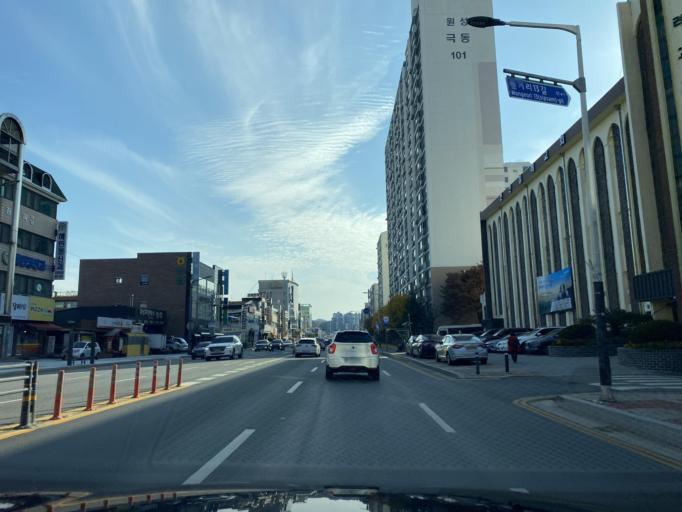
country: KR
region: Chungcheongnam-do
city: Cheonan
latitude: 36.8033
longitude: 127.1589
